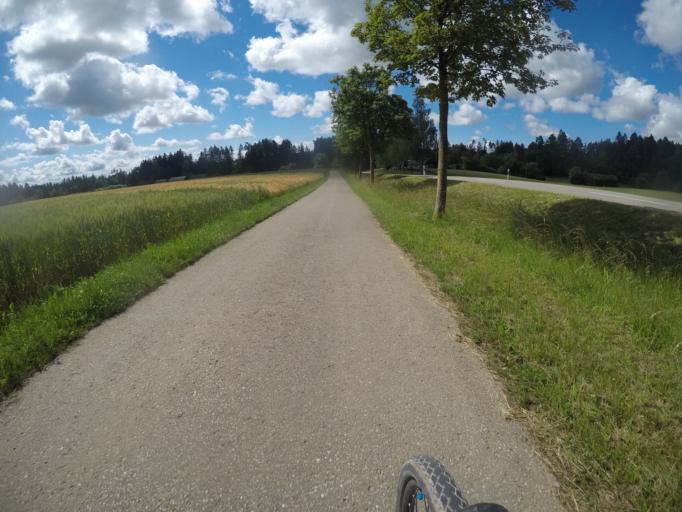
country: DE
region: Baden-Wuerttemberg
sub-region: Regierungsbezirk Stuttgart
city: Unterjettingen
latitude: 48.5517
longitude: 8.7823
